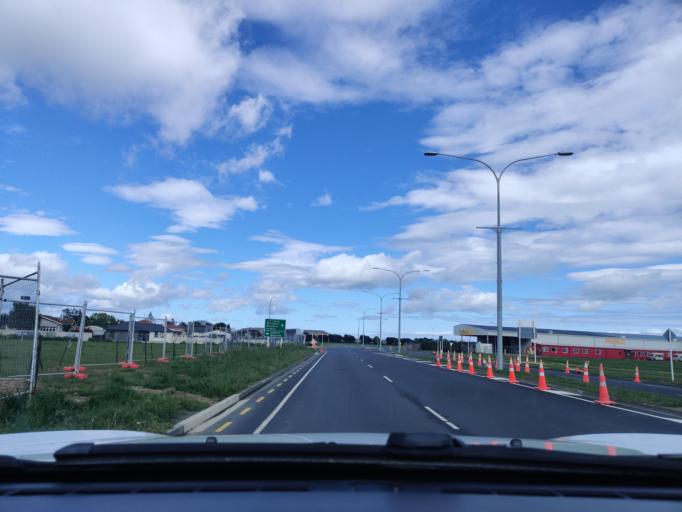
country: NZ
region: Manawatu-Wanganui
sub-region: Palmerston North City
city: Palmerston North
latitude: -40.3262
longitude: 175.6206
